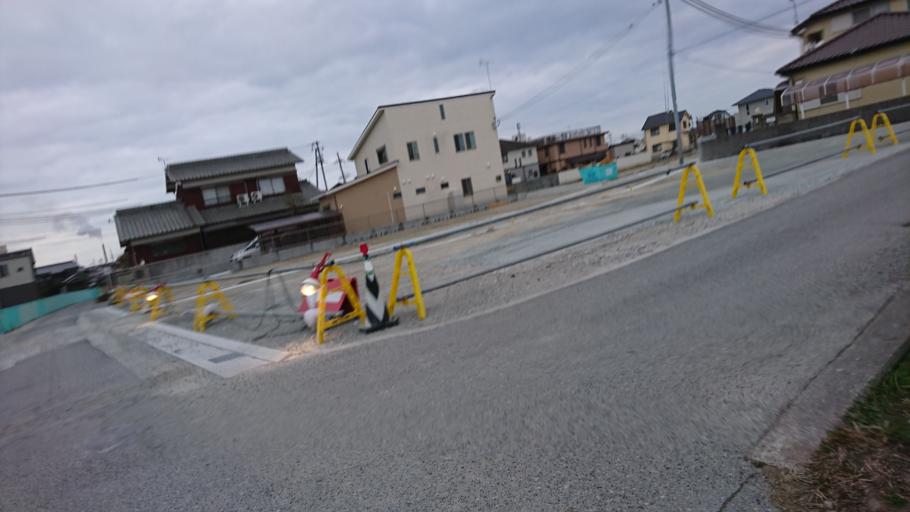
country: JP
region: Hyogo
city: Kakogawacho-honmachi
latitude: 34.7426
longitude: 134.8540
